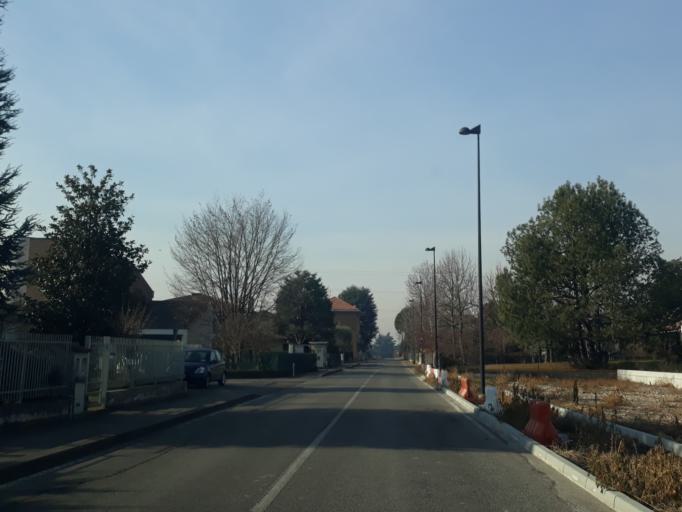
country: IT
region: Lombardy
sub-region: Provincia di Monza e Brianza
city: Bellusco
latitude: 45.6223
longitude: 9.4142
